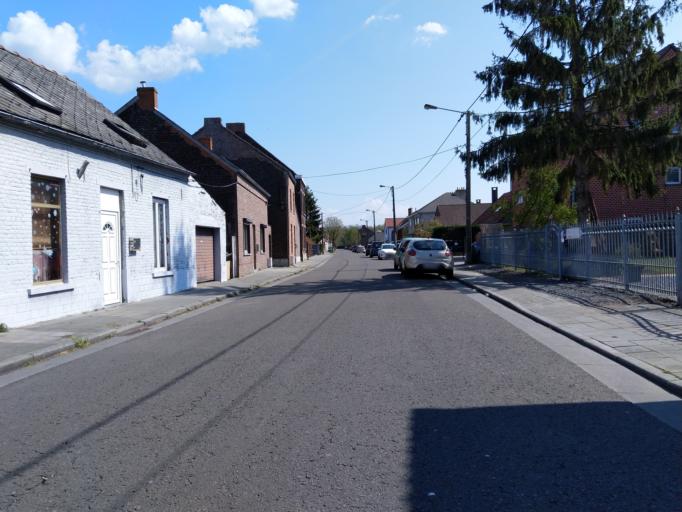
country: BE
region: Wallonia
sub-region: Province du Hainaut
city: Mons
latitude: 50.4740
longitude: 3.9153
